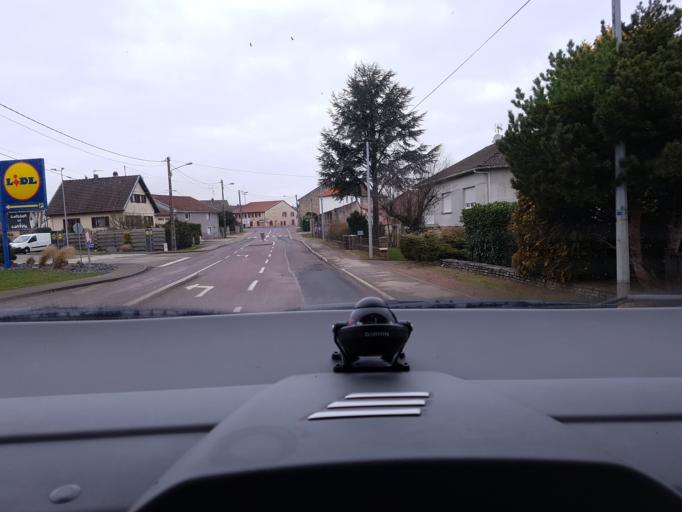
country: FR
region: Lorraine
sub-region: Departement de la Moselle
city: Morhange
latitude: 48.9314
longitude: 6.6120
